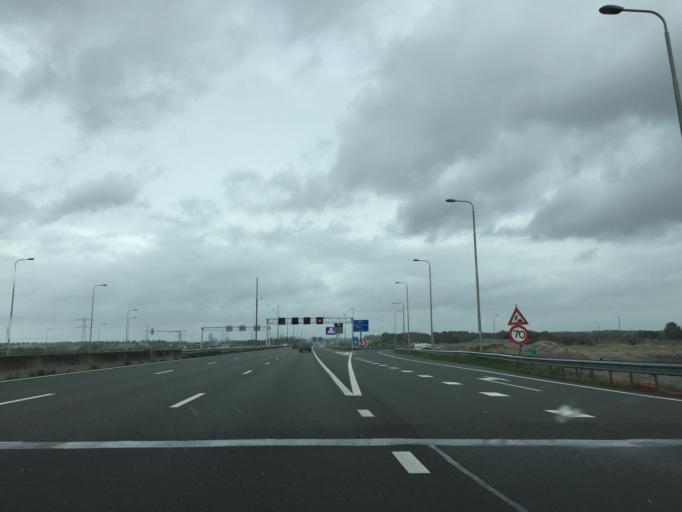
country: NL
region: North Holland
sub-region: Gemeente Naarden
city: Naarden
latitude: 52.3324
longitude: 5.1522
